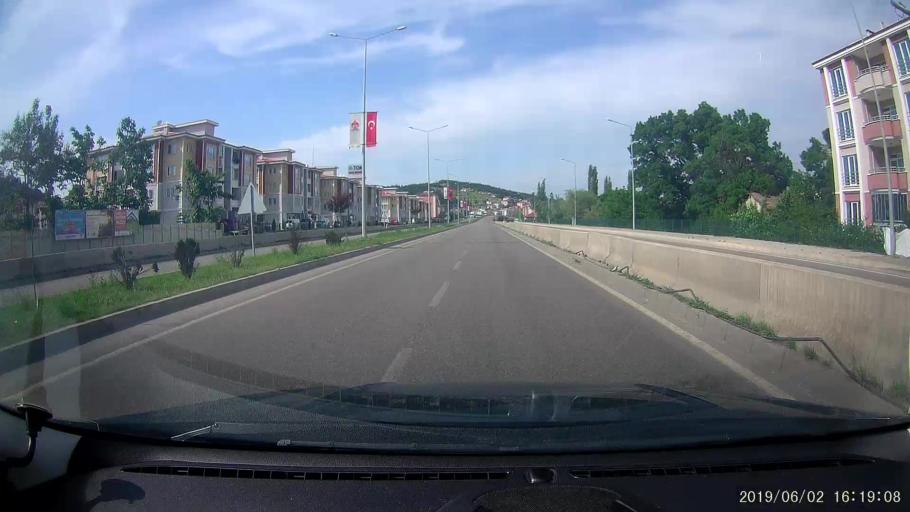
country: TR
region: Samsun
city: Havza
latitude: 40.9637
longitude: 35.6672
